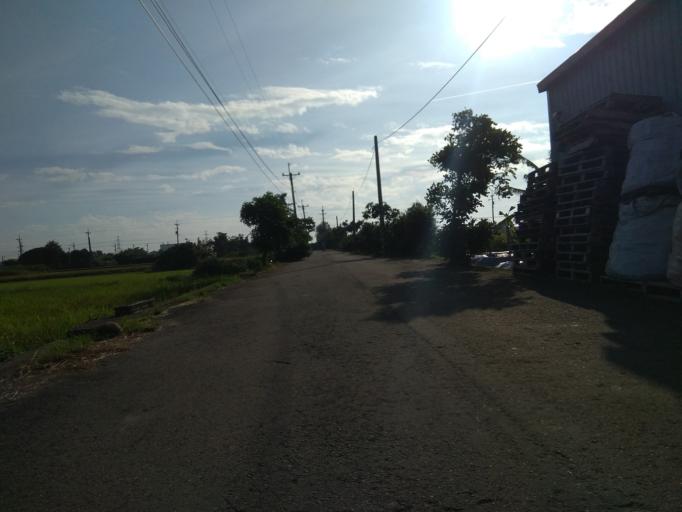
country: TW
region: Taiwan
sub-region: Hsinchu
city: Zhubei
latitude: 24.9812
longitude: 121.0571
